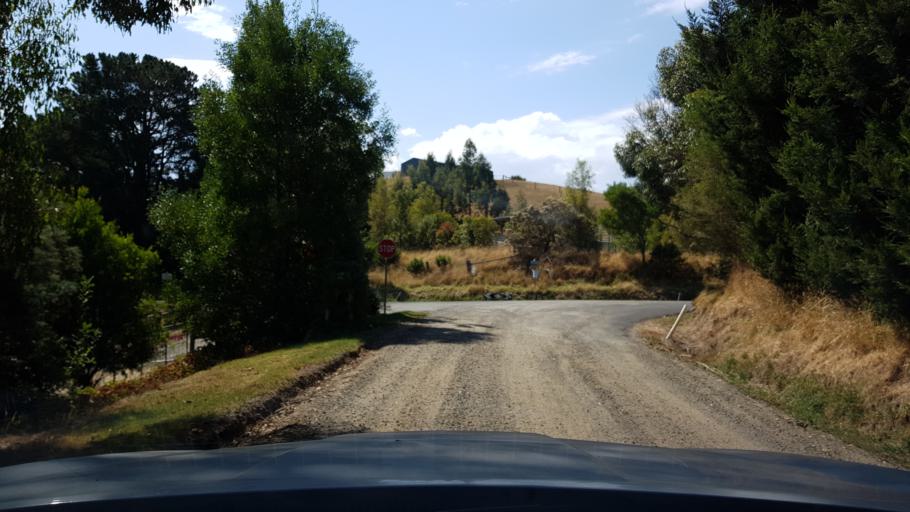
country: AU
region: Victoria
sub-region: Baw Baw
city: Warragul
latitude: -38.2801
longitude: 145.9326
